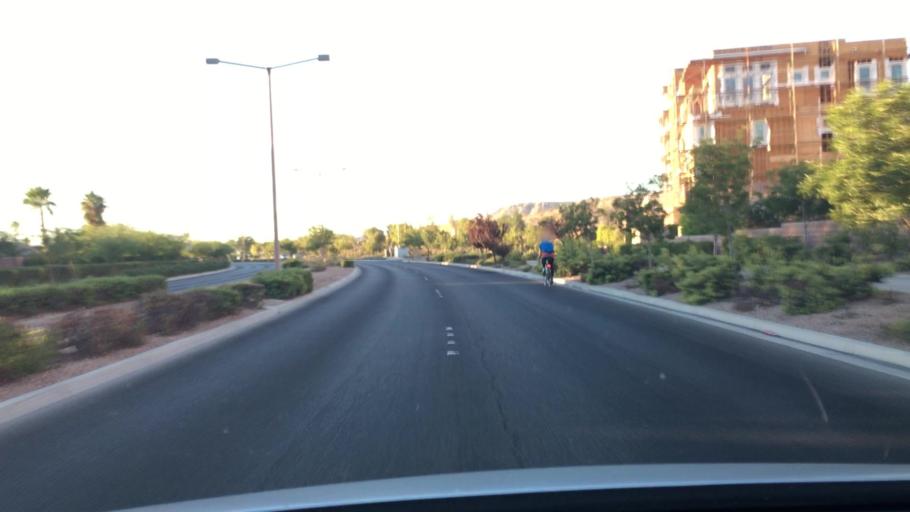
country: US
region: Nevada
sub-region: Clark County
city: Summerlin South
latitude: 36.1116
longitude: -115.3299
